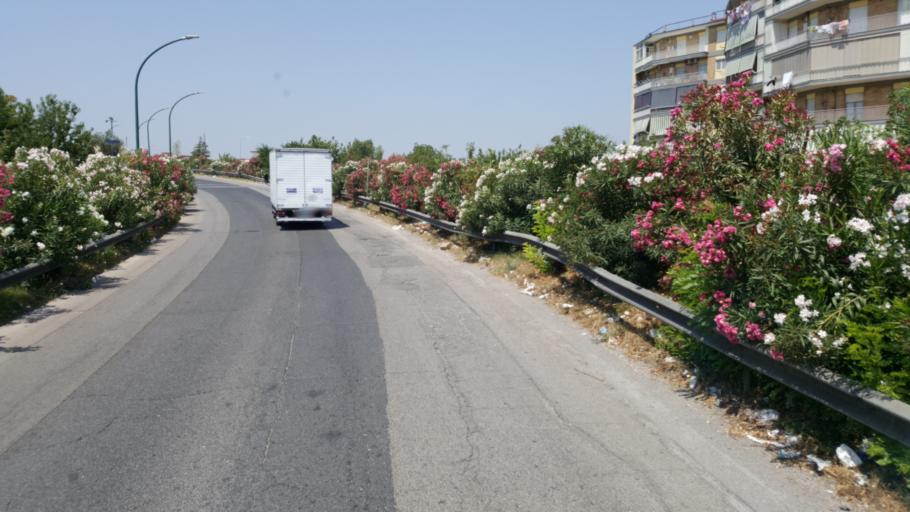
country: IT
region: Campania
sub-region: Provincia di Napoli
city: Arpino
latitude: 40.8825
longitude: 14.3172
